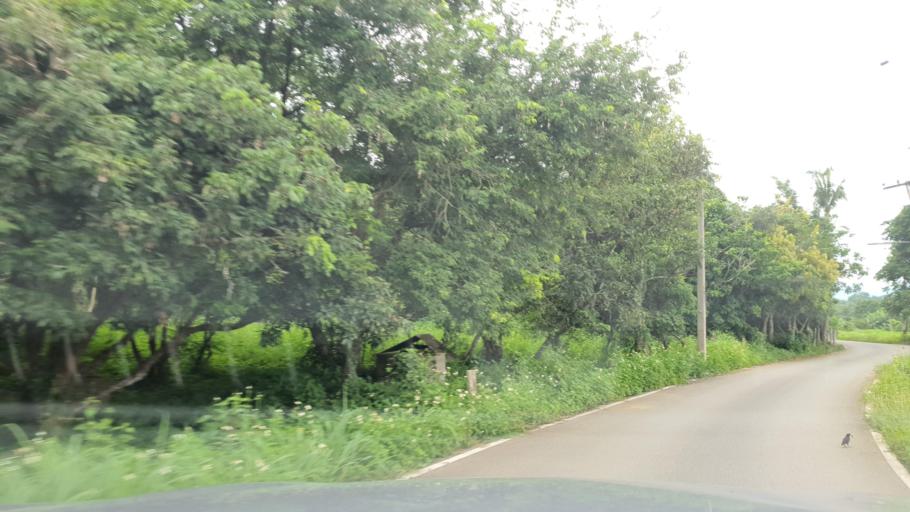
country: TH
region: Chiang Mai
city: San Sai
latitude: 18.9273
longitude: 98.9147
